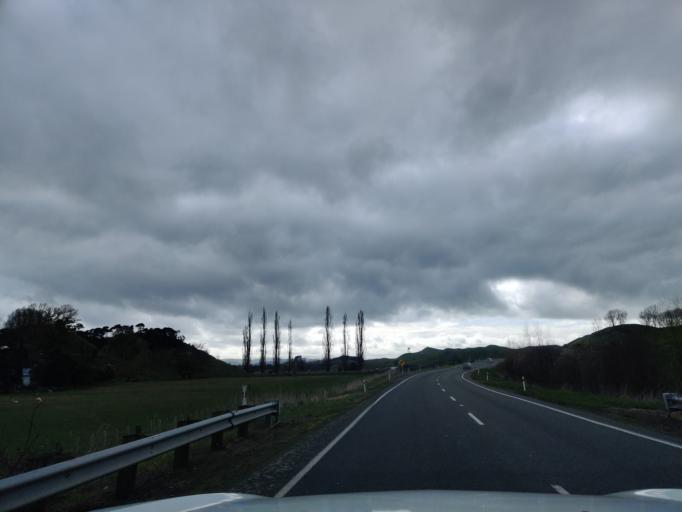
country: NZ
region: Manawatu-Wanganui
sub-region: Rangitikei District
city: Bulls
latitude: -39.9241
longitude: 175.5885
